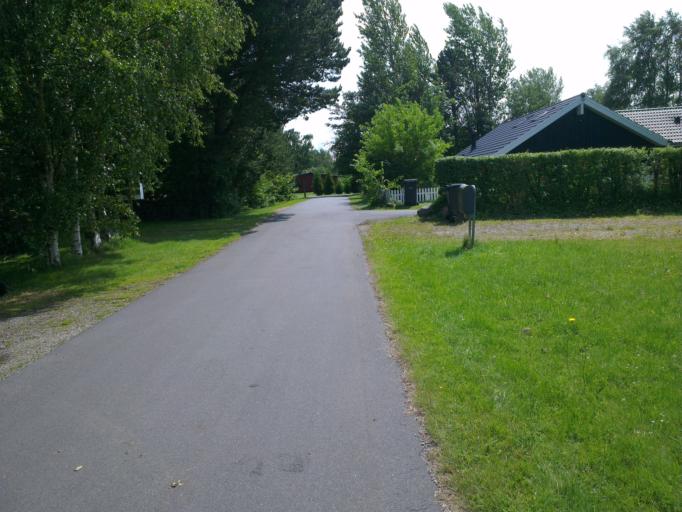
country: DK
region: Capital Region
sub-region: Halsnaes Kommune
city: Hundested
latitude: 55.9181
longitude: 11.9121
